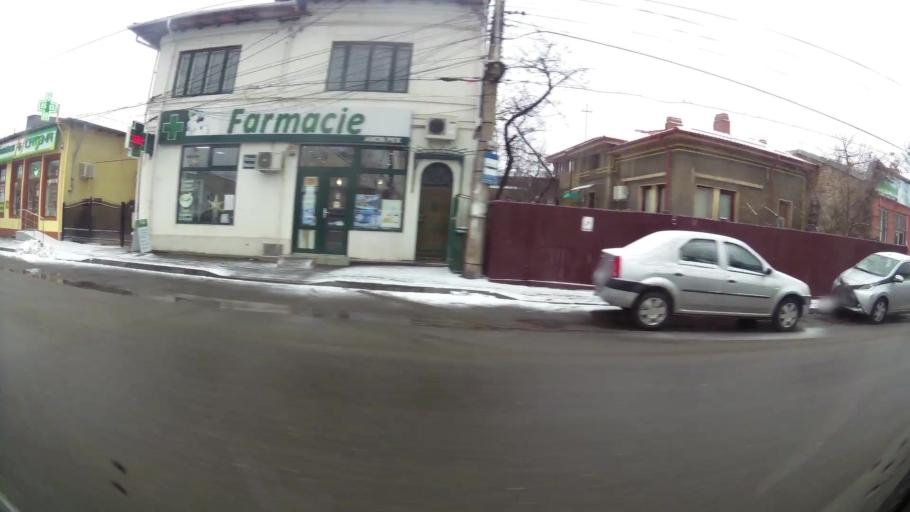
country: RO
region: Prahova
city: Ploiesti
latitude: 44.9326
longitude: 26.0199
